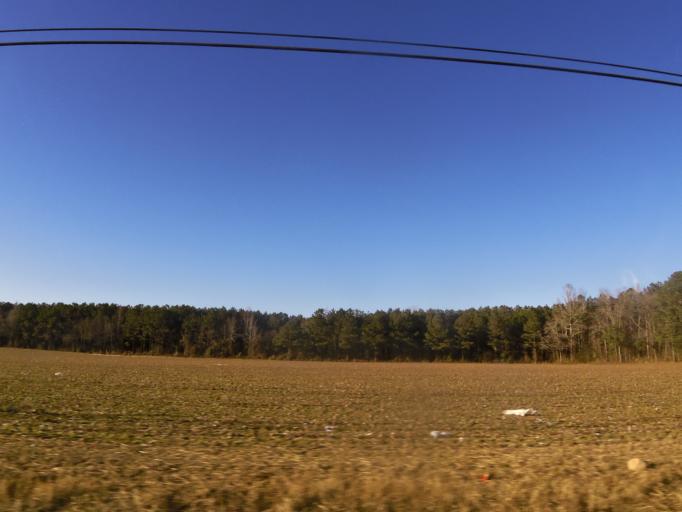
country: US
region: Virginia
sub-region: Isle of Wight County
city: Windsor
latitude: 36.6885
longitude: -76.7568
